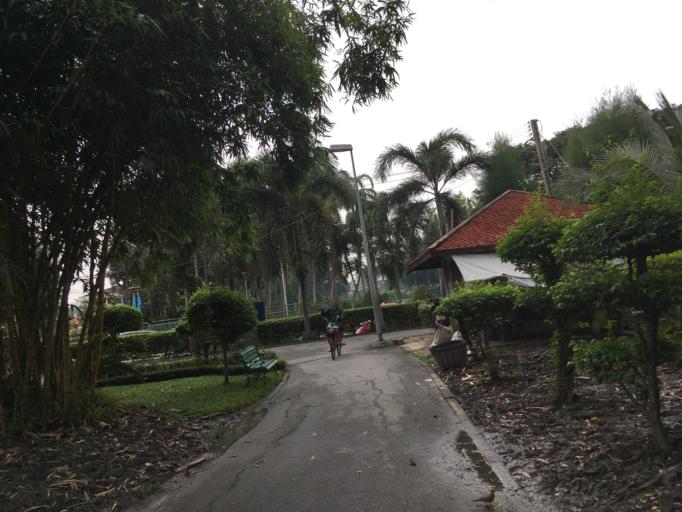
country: TH
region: Bangkok
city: Bueng Kum
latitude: 13.7880
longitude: 100.6739
